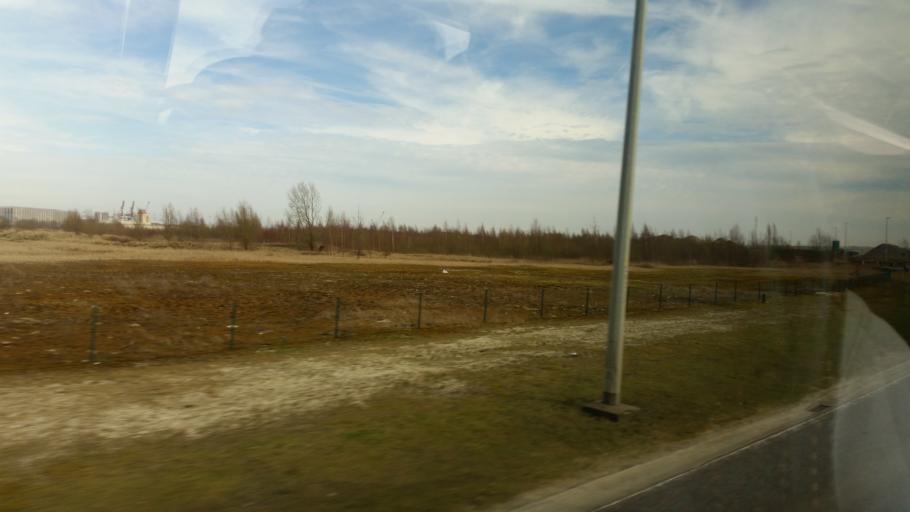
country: BE
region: Flanders
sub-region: Provincie Oost-Vlaanderen
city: Beveren
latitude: 51.2562
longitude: 4.2044
